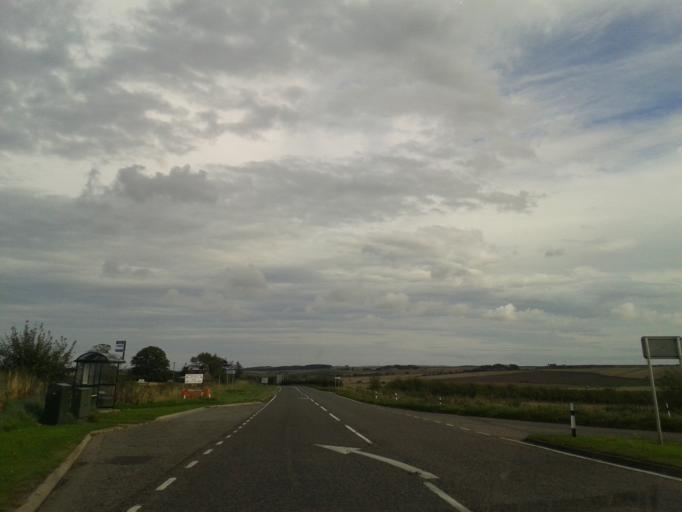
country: GB
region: Scotland
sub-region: Aberdeenshire
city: Whitehills
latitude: 57.6498
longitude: -2.6395
